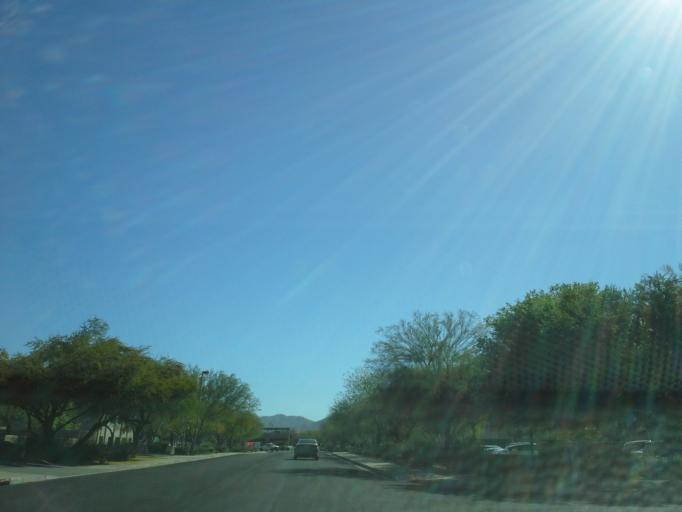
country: US
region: Arizona
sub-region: Maricopa County
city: Paradise Valley
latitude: 33.6165
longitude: -111.9000
